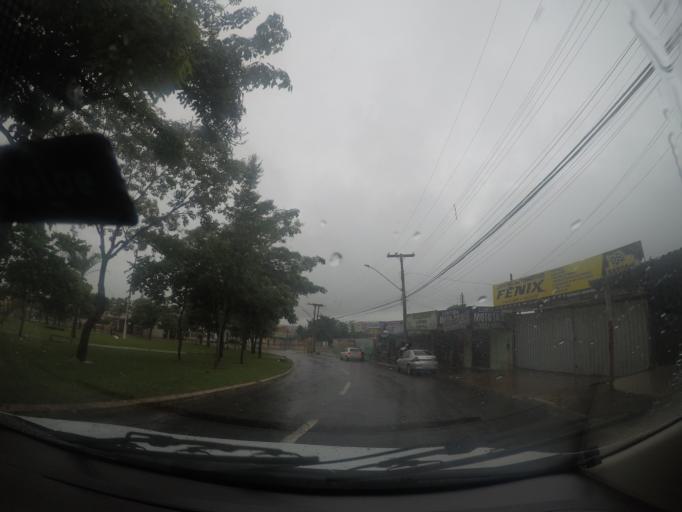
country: BR
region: Goias
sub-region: Goiania
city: Goiania
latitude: -16.6052
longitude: -49.3357
